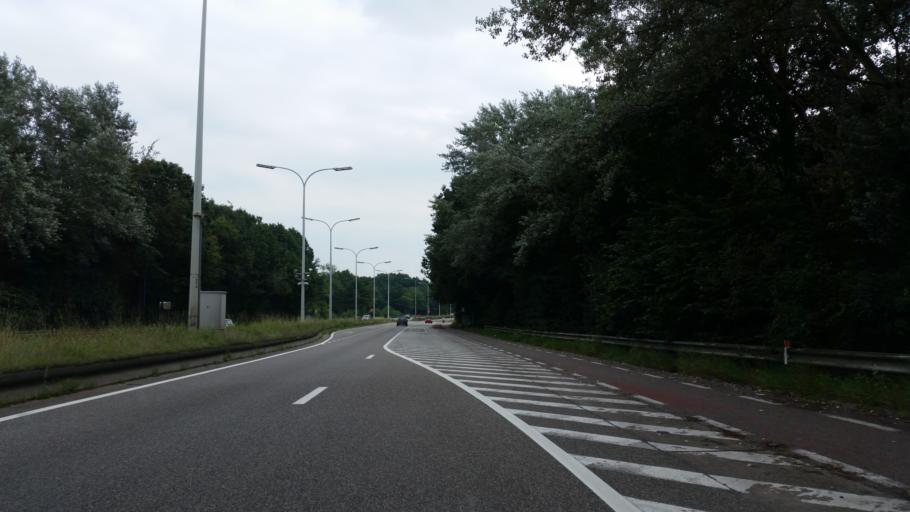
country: BE
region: Flanders
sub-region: Provincie Antwerpen
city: Turnhout
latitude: 51.2958
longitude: 4.9526
